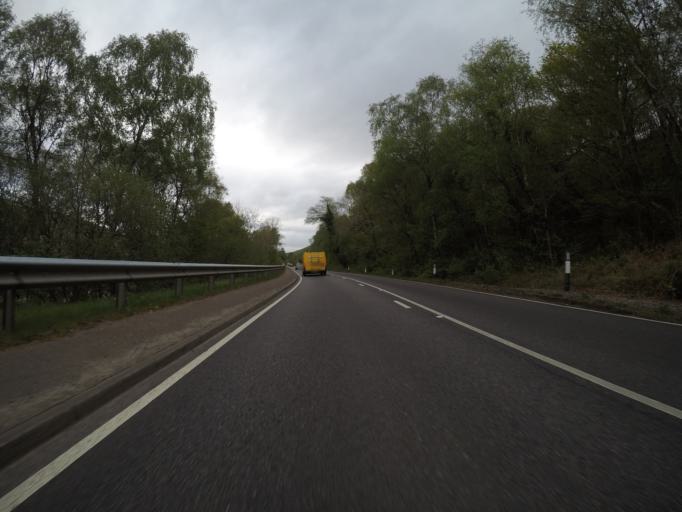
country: GB
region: Scotland
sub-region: Highland
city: Fort William
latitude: 56.7845
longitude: -5.1570
